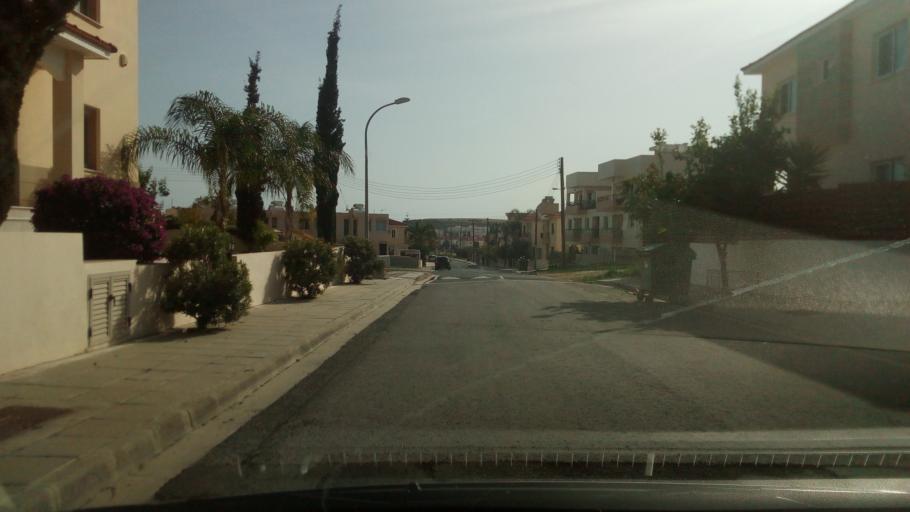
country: CY
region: Larnaka
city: Voroklini
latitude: 34.9785
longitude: 33.6497
